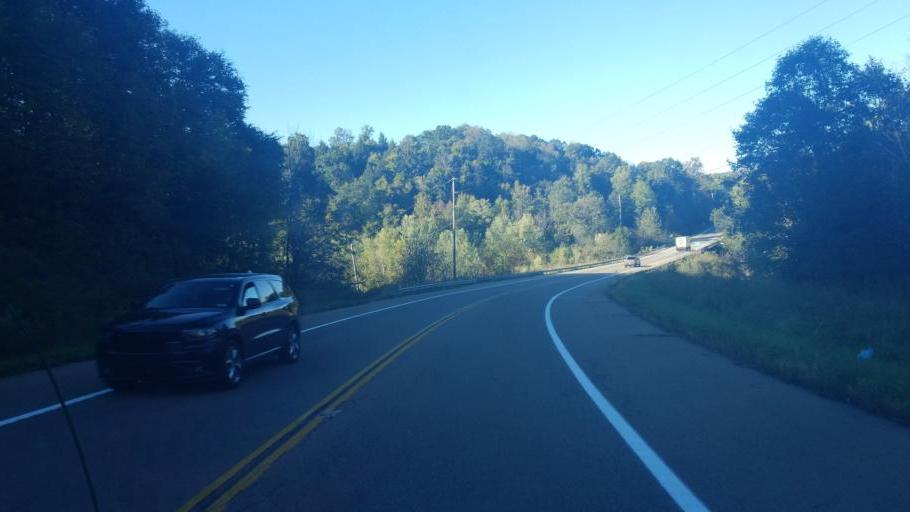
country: US
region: Ohio
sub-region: Columbiana County
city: Glenmoor
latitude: 40.7164
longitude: -80.6350
